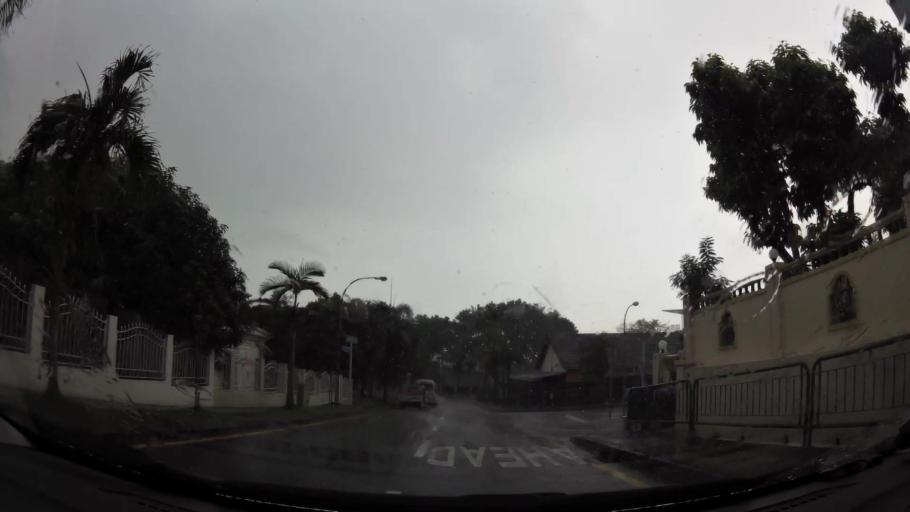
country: SG
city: Singapore
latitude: 1.3375
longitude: 103.9559
